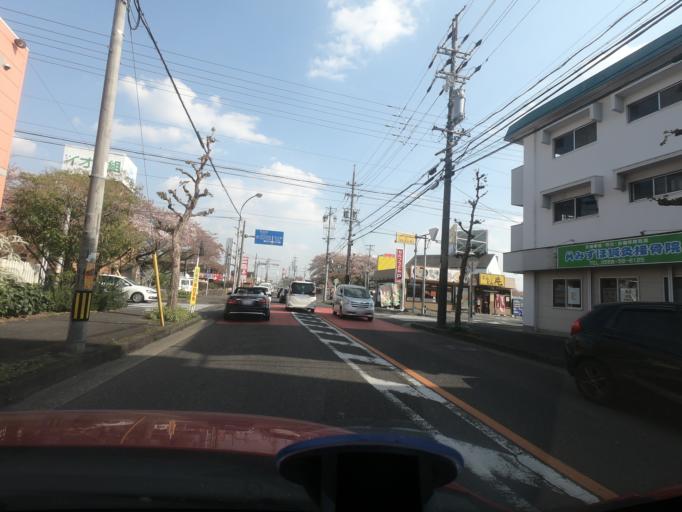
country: JP
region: Aichi
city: Kasugai
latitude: 35.2439
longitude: 136.9651
